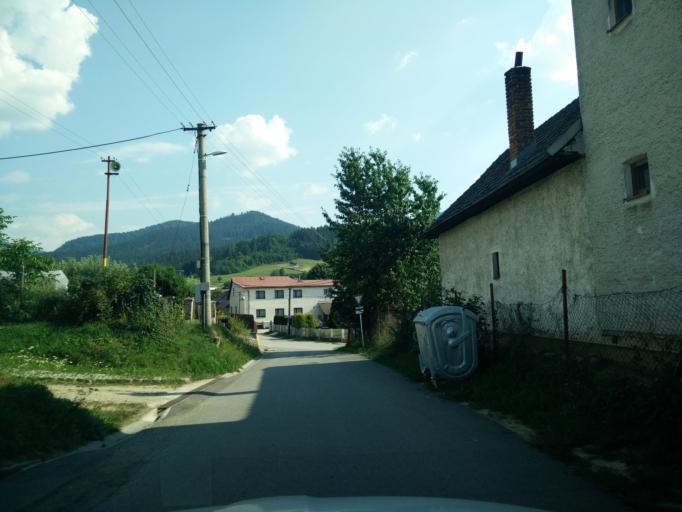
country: SK
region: Zilinsky
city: Rajec
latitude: 49.0996
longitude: 18.7100
